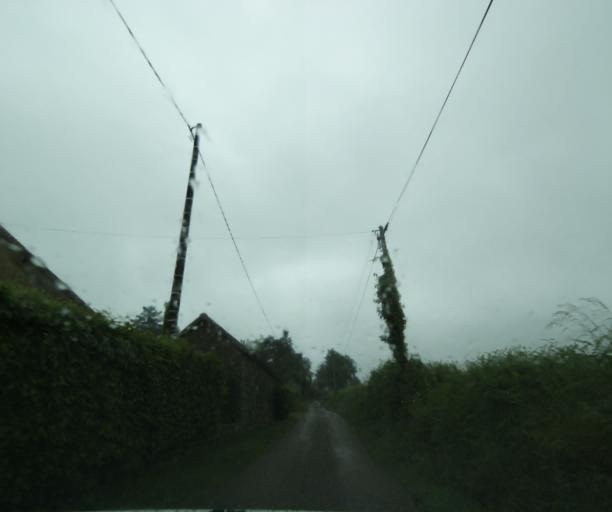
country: FR
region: Bourgogne
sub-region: Departement de Saone-et-Loire
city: Charolles
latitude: 46.3739
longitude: 4.3474
